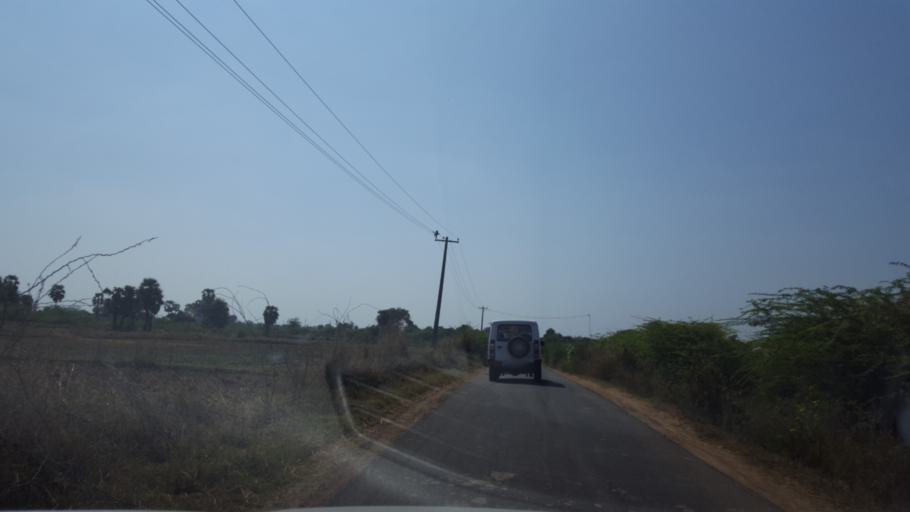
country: IN
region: Tamil Nadu
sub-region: Kancheepuram
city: Wallajahbad
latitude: 12.8583
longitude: 79.7825
